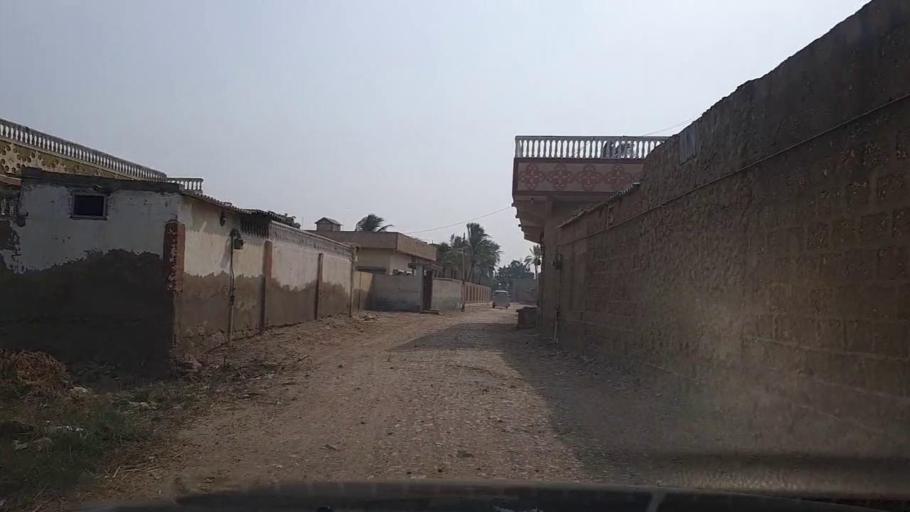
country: PK
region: Sindh
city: Thatta
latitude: 24.5557
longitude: 67.8377
